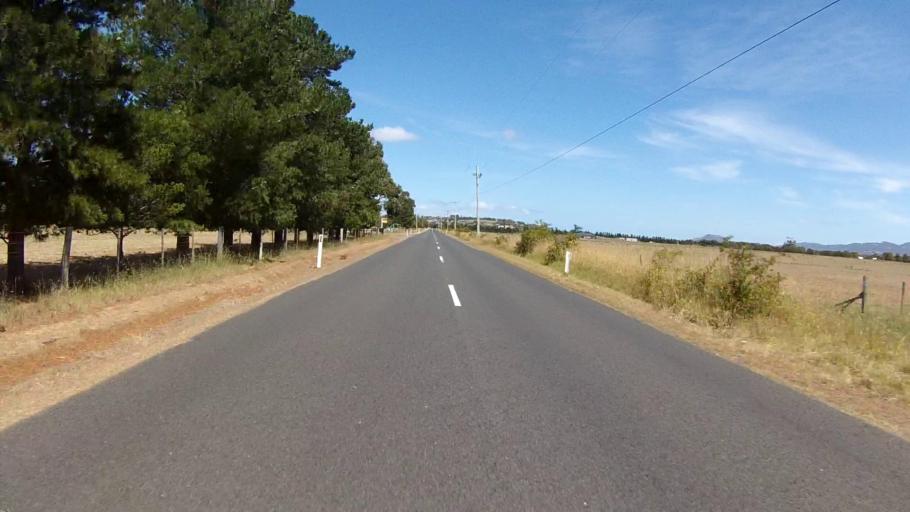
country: AU
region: Tasmania
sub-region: Sorell
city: Sorell
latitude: -42.7719
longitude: 147.5179
